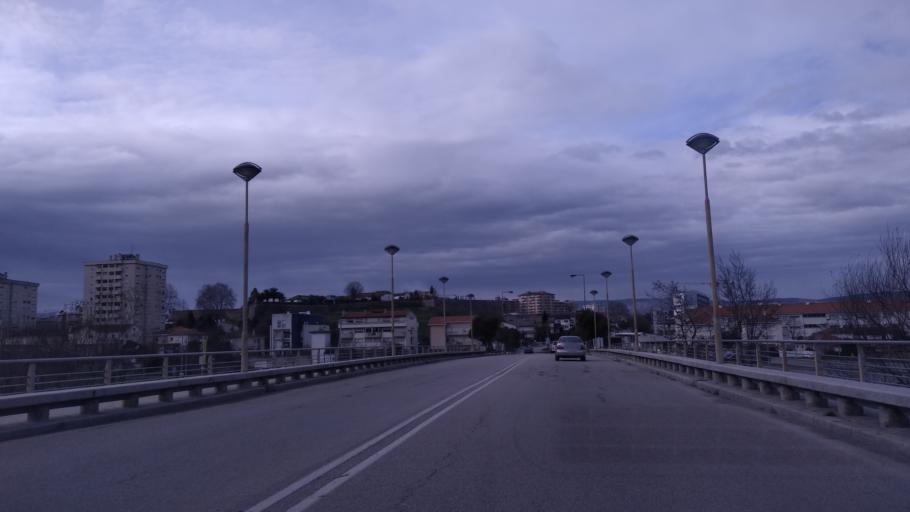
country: PT
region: Vila Real
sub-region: Chaves
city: Chaves
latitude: 41.7416
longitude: -7.4636
